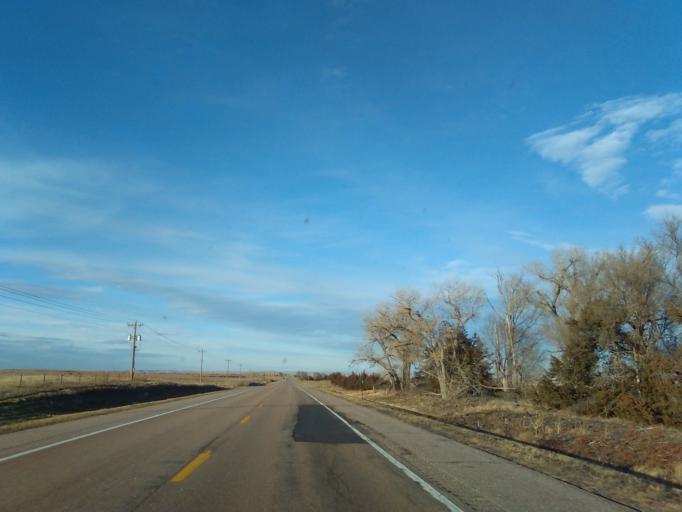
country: US
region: Nebraska
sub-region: Morrill County
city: Bridgeport
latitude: 41.5323
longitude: -102.9844
